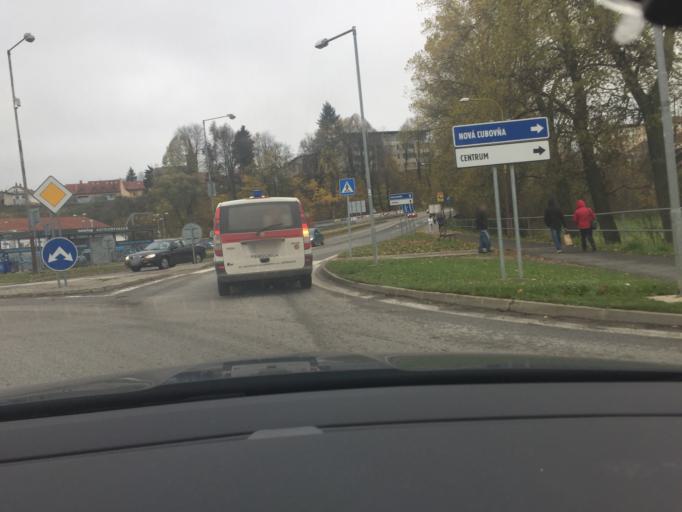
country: SK
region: Presovsky
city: Stara L'ubovna
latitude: 49.3050
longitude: 20.6873
